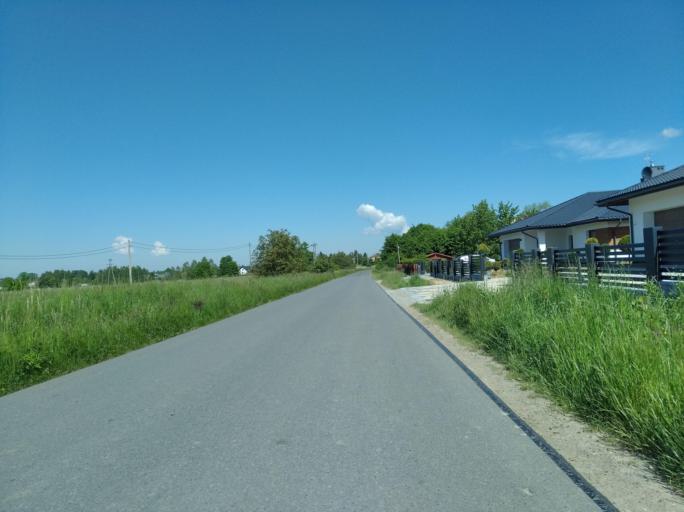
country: PL
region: Subcarpathian Voivodeship
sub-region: Powiat krosnienski
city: Odrzykon
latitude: 49.7344
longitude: 21.7446
